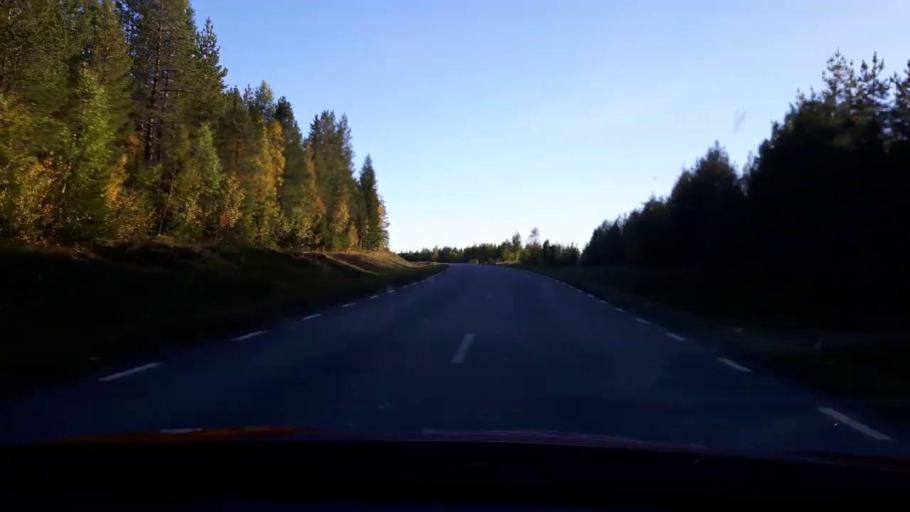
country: SE
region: Jaemtland
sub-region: OEstersunds Kommun
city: Lit
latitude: 63.7586
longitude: 14.7170
